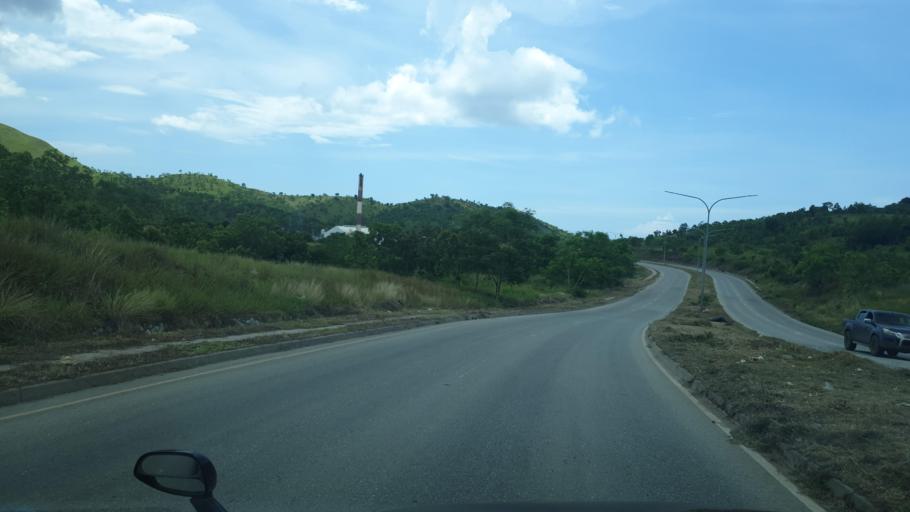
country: PG
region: National Capital
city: Port Moresby
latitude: -9.4263
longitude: 147.1410
